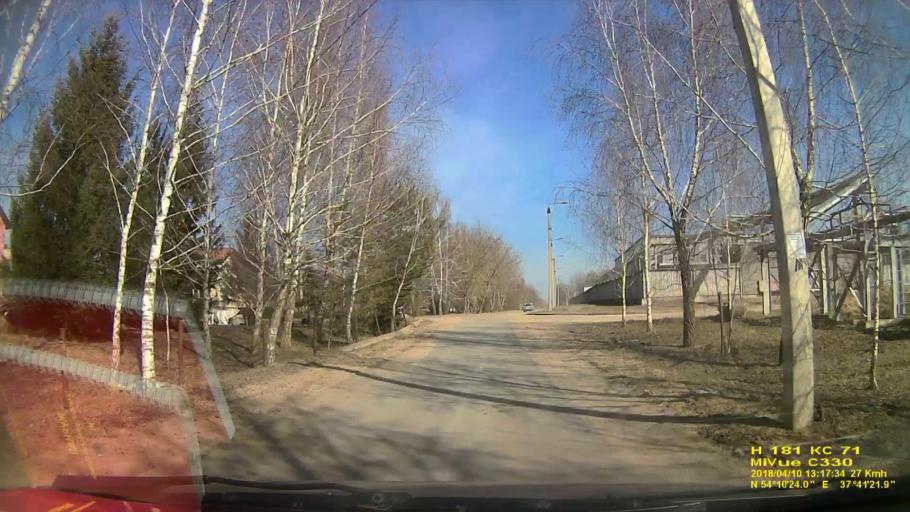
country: RU
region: Tula
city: Tula
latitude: 54.1733
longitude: 37.6895
